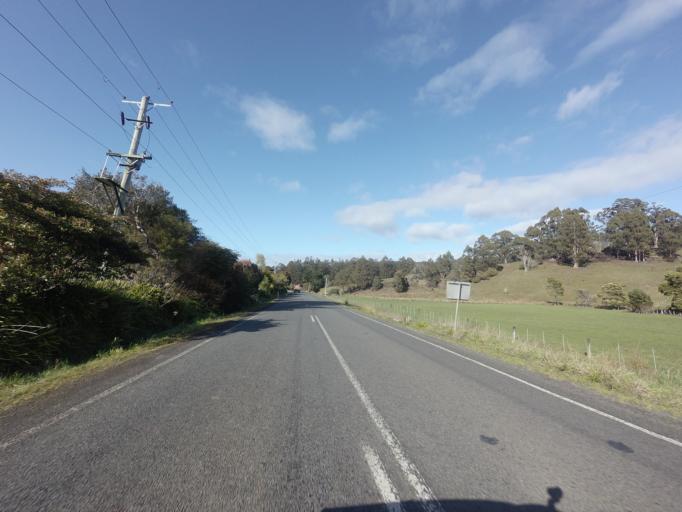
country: AU
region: Tasmania
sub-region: Huon Valley
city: Cygnet
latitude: -43.2684
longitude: 147.0109
